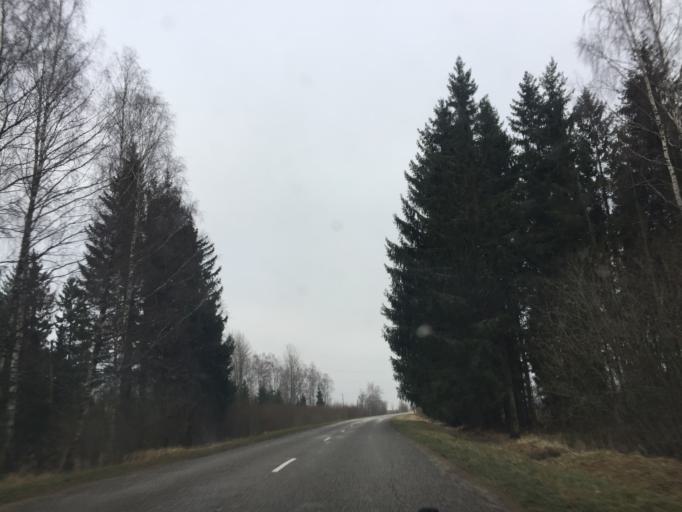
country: LV
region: Limbazu Rajons
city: Limbazi
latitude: 57.5793
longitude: 24.6621
